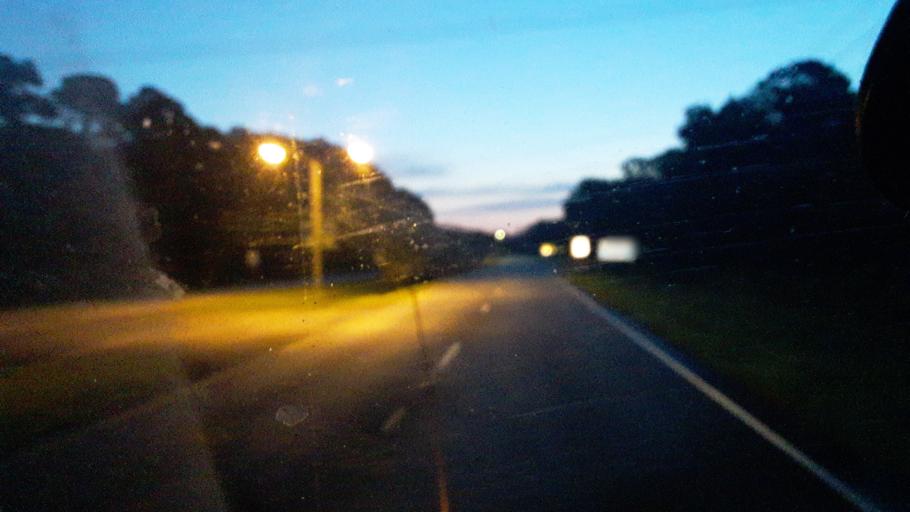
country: US
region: South Carolina
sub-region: Horry County
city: Little River
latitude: 33.8793
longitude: -78.6061
